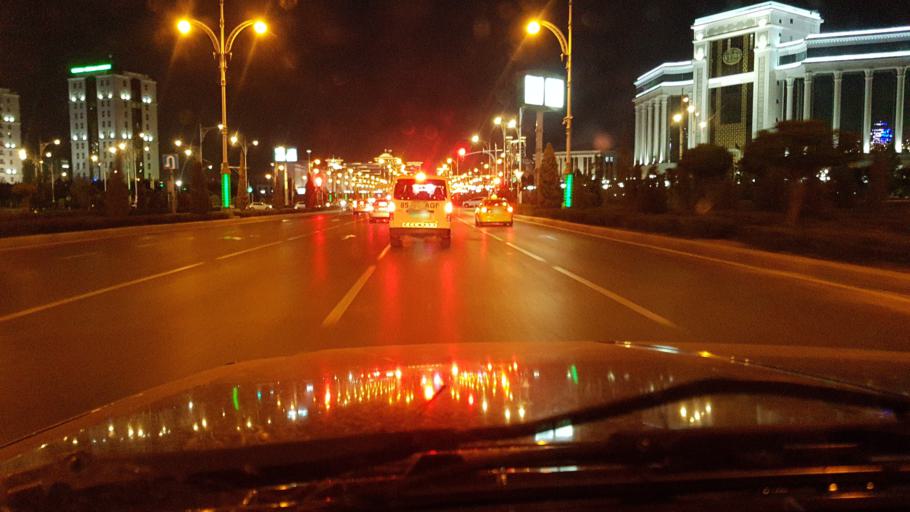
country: TM
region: Ahal
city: Ashgabat
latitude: 37.8987
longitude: 58.3591
